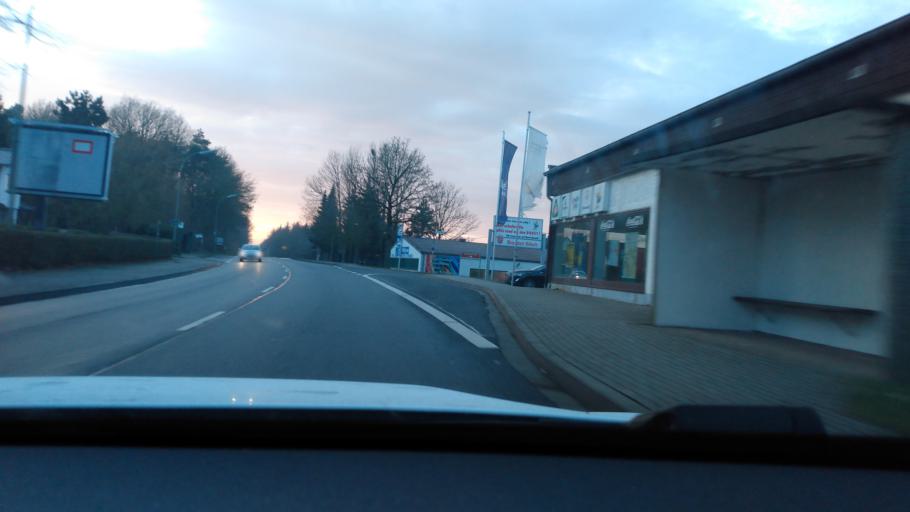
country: DE
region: Rheinland-Pfalz
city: Kircheib
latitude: 50.7095
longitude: 7.4510
